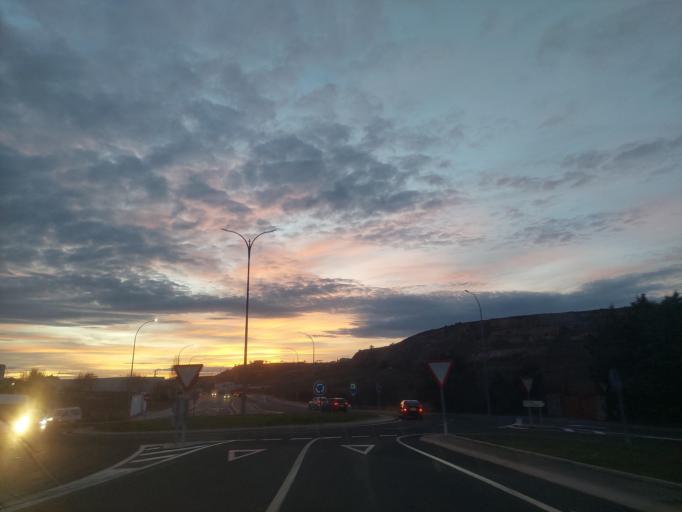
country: ES
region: Castille and Leon
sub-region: Provincia de Segovia
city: La Lastrilla
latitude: 40.9725
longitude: -4.0886
